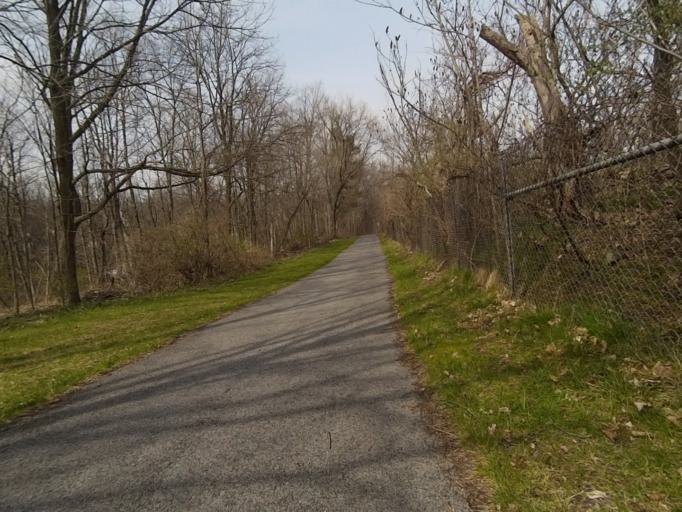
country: US
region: Pennsylvania
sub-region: Centre County
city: Lemont
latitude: 40.8033
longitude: -77.8274
